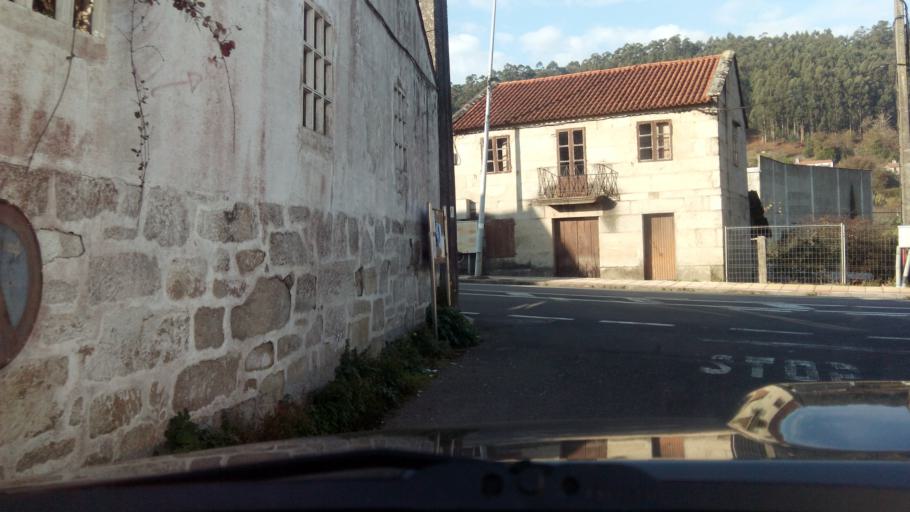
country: ES
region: Galicia
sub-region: Provincia de Pontevedra
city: Marin
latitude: 42.3627
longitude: -8.7371
